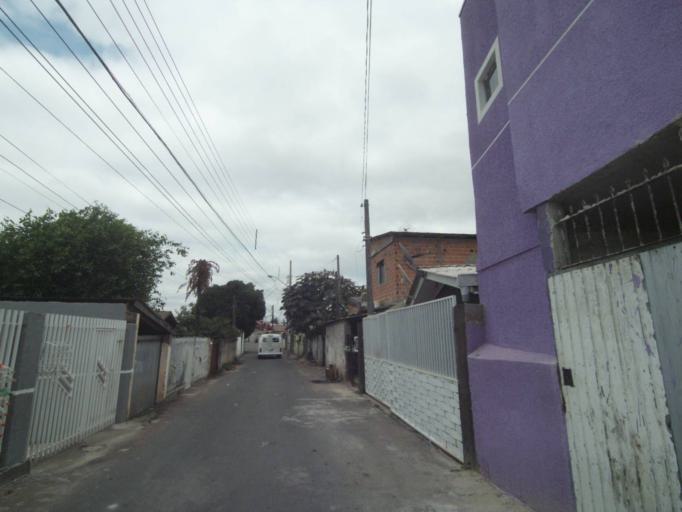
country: BR
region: Parana
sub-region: Sao Jose Dos Pinhais
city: Sao Jose dos Pinhais
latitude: -25.5367
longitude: -49.2662
